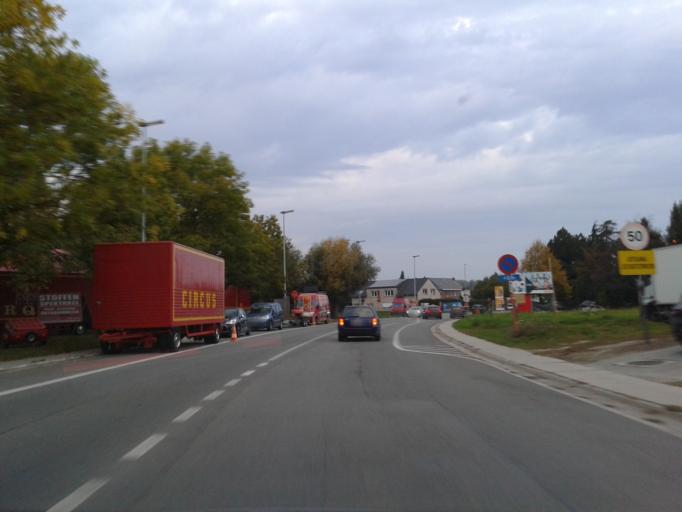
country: BE
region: Flanders
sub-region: Provincie Oost-Vlaanderen
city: Lebbeke
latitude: 51.0011
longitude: 4.1234
